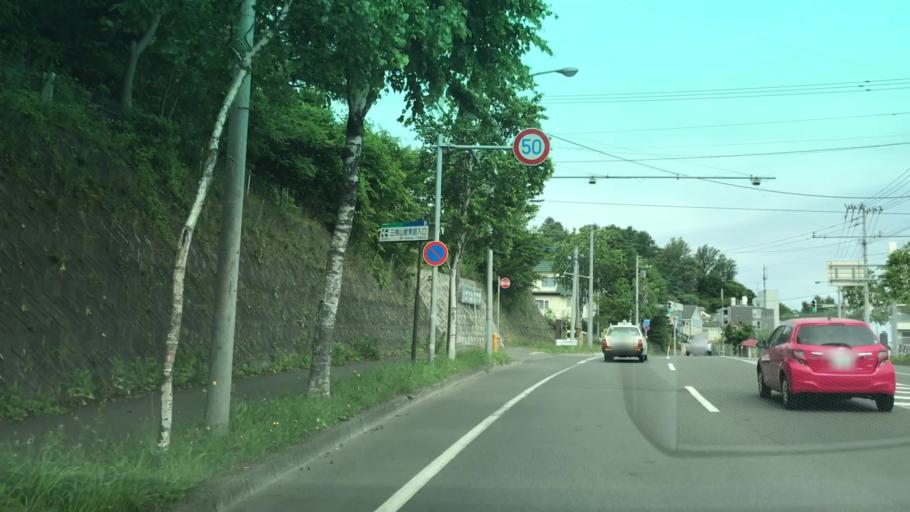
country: JP
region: Hokkaido
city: Sapporo
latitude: 43.0647
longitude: 141.2896
